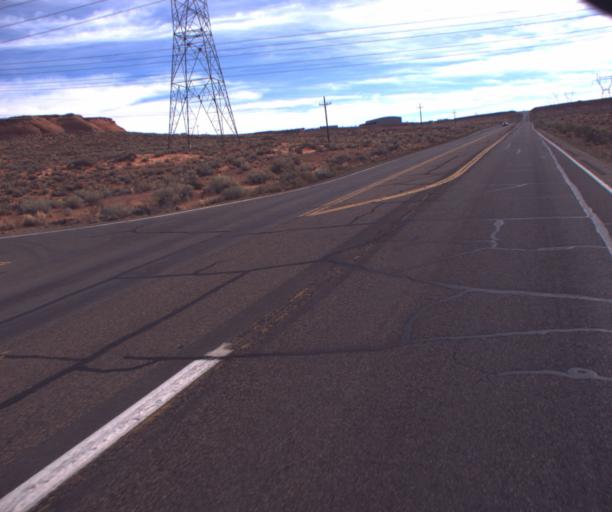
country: US
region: Arizona
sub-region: Coconino County
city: LeChee
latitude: 36.8964
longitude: -111.4001
